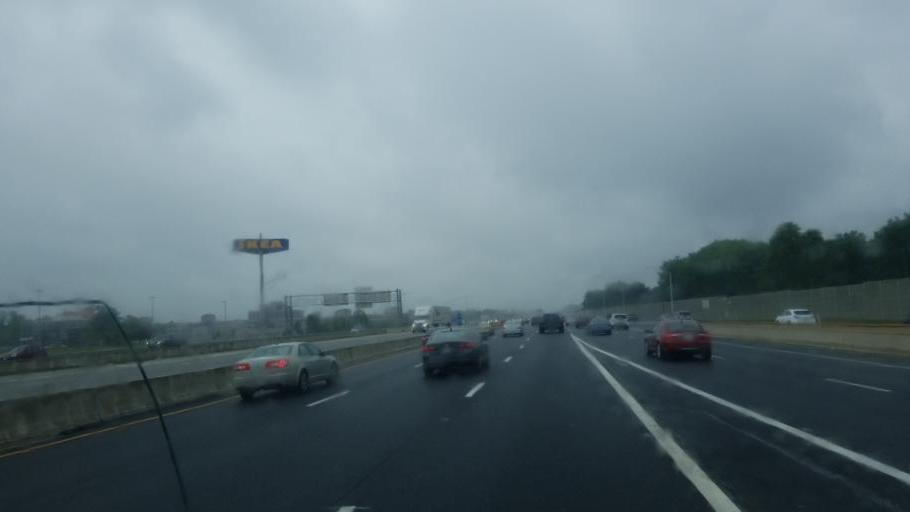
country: US
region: Indiana
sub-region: Hamilton County
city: Fishers
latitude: 39.9545
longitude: -86.0098
